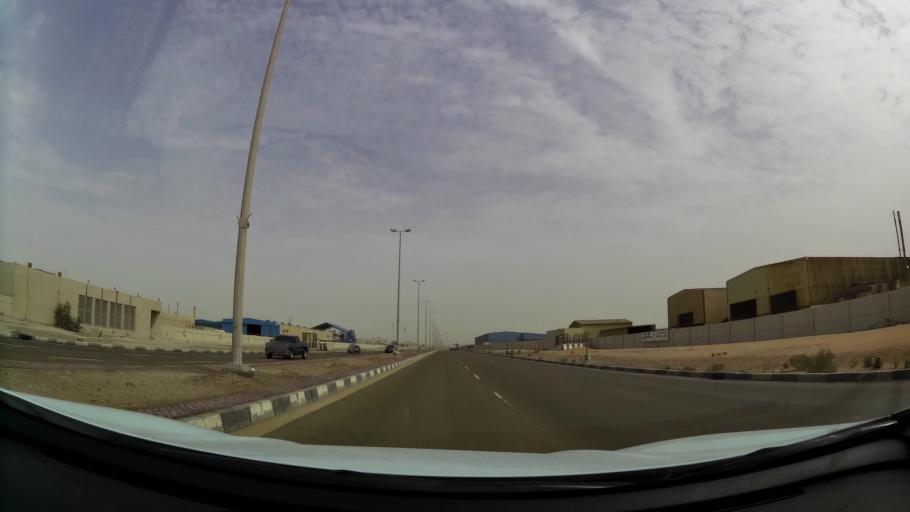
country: AE
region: Abu Dhabi
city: Abu Dhabi
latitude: 24.3227
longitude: 54.4884
